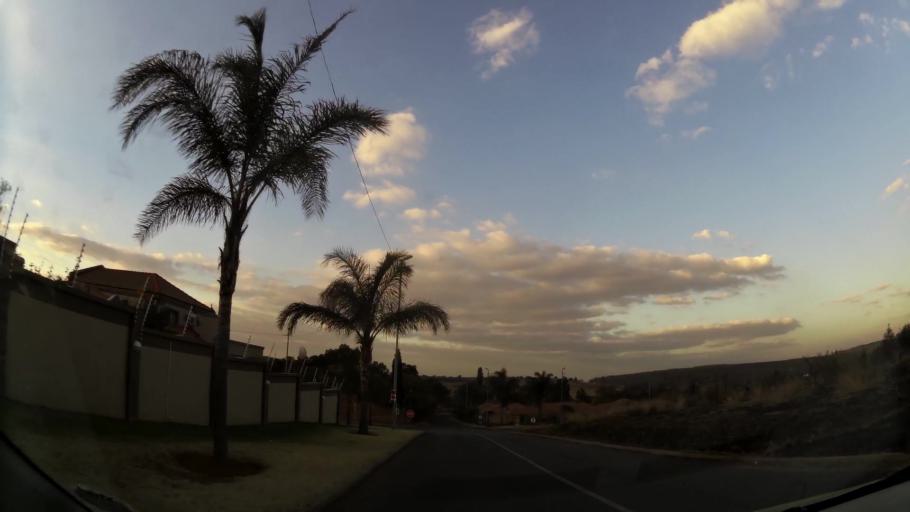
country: ZA
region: Gauteng
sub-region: West Rand District Municipality
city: Krugersdorp
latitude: -26.0699
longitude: 27.7913
